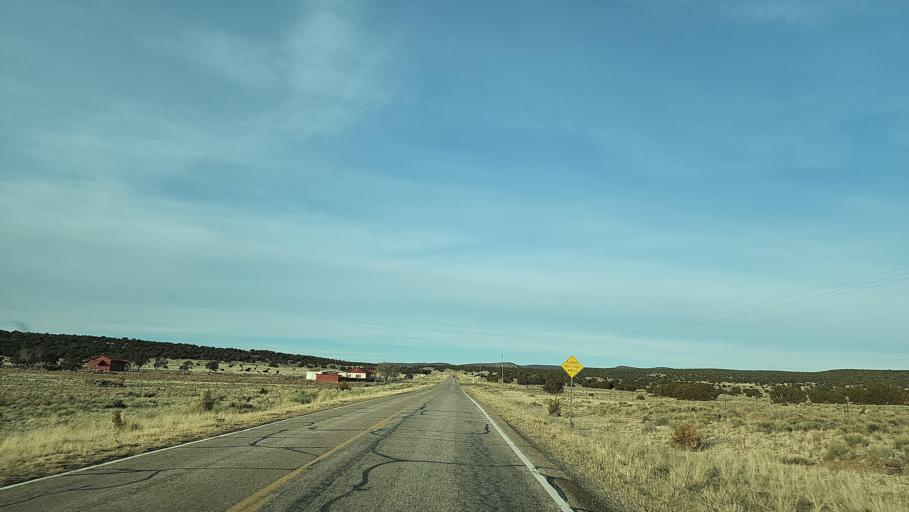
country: US
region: New Mexico
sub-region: Catron County
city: Reserve
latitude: 34.3986
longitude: -108.4434
